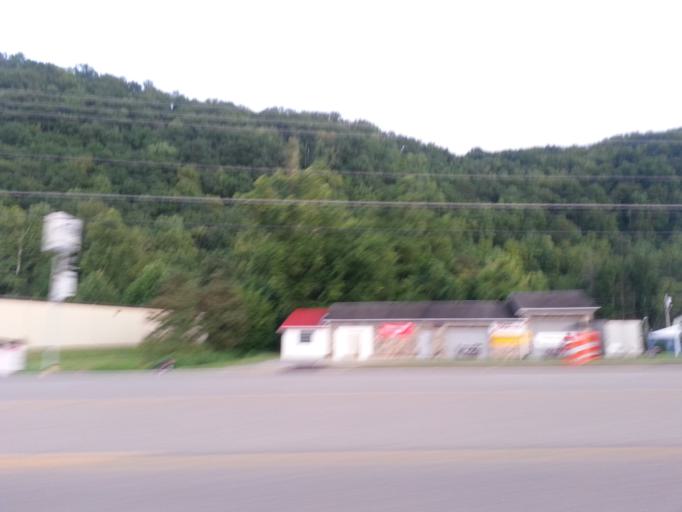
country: US
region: Tennessee
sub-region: Carter County
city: Hunter
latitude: 36.3795
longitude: -82.1499
